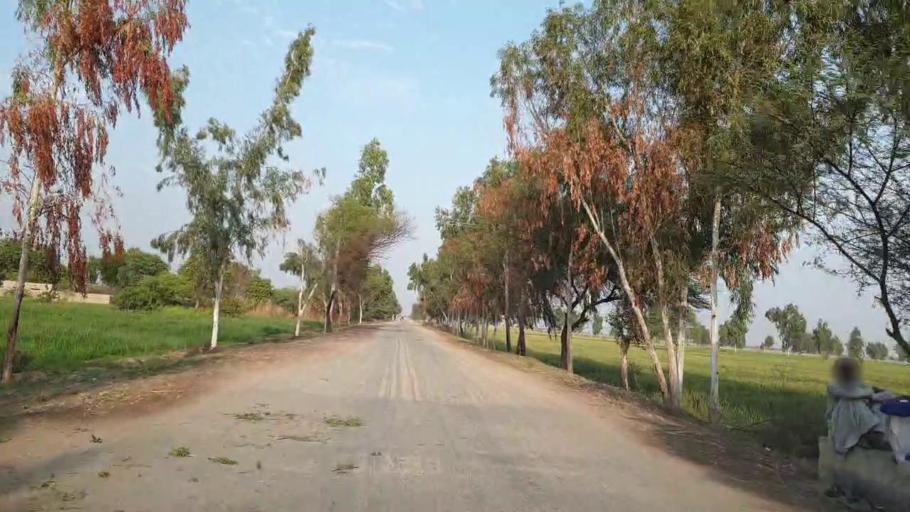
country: PK
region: Sindh
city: Pithoro
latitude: 25.5816
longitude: 69.2642
